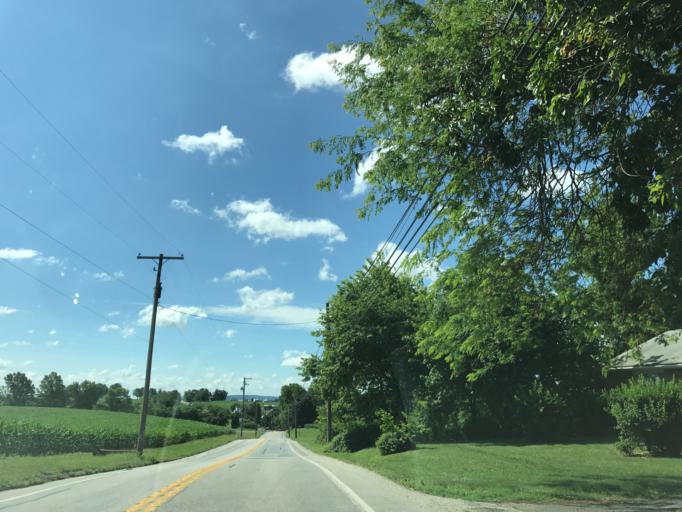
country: US
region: Pennsylvania
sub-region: Lancaster County
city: Elizabethtown
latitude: 40.1355
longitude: -76.6007
